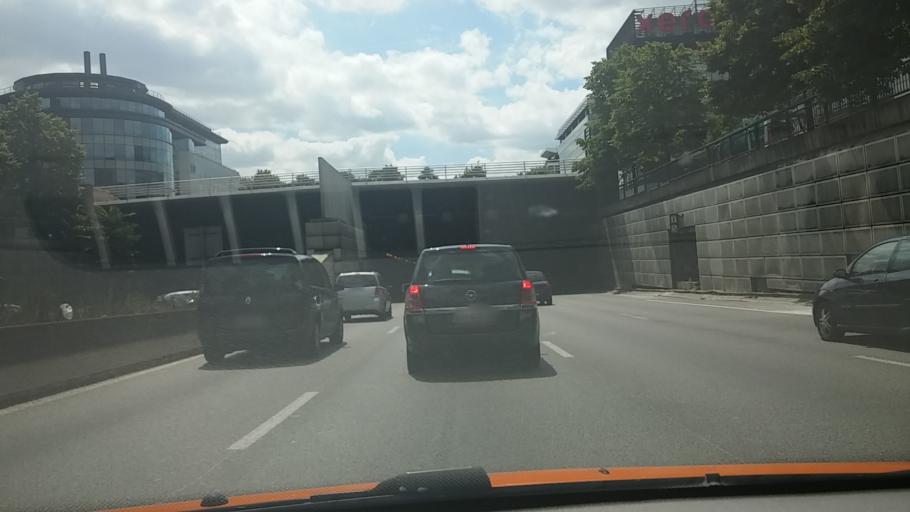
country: FR
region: Ile-de-France
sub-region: Departement de Seine-Saint-Denis
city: Saint-Denis
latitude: 48.9190
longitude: 2.3572
